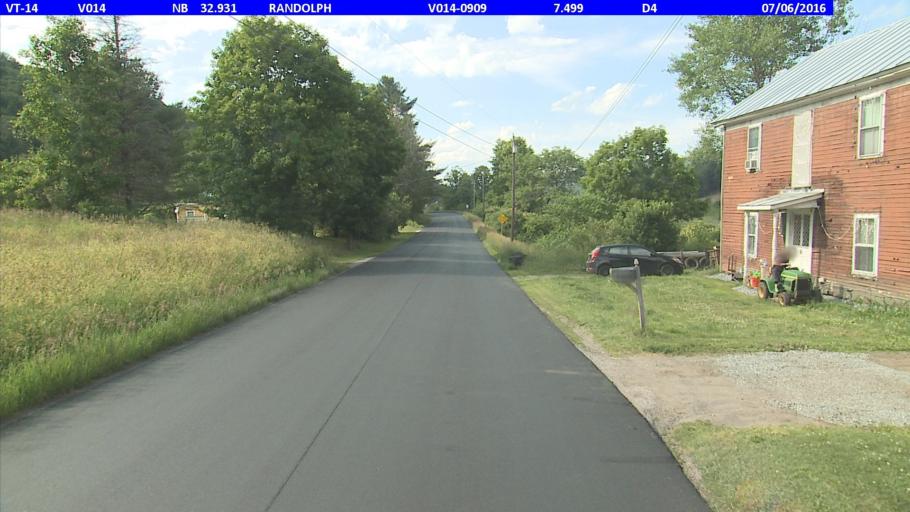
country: US
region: Vermont
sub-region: Orange County
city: Chelsea
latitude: 43.9758
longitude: -72.5558
